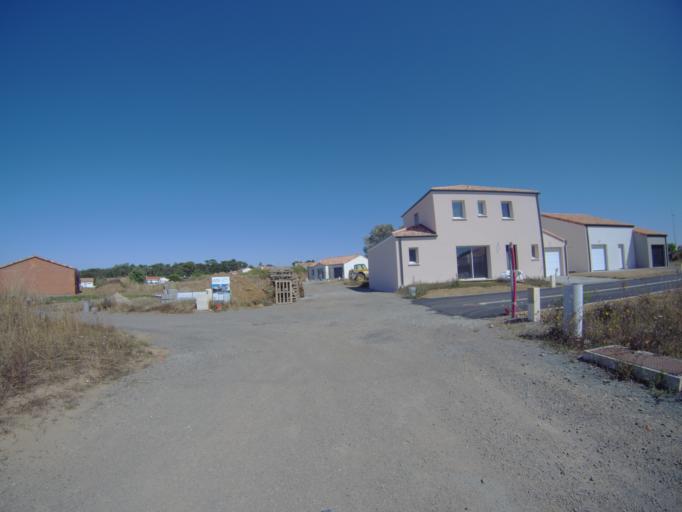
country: FR
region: Pays de la Loire
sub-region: Departement de la Vendee
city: Jard-sur-Mer
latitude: 46.4092
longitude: -1.5491
